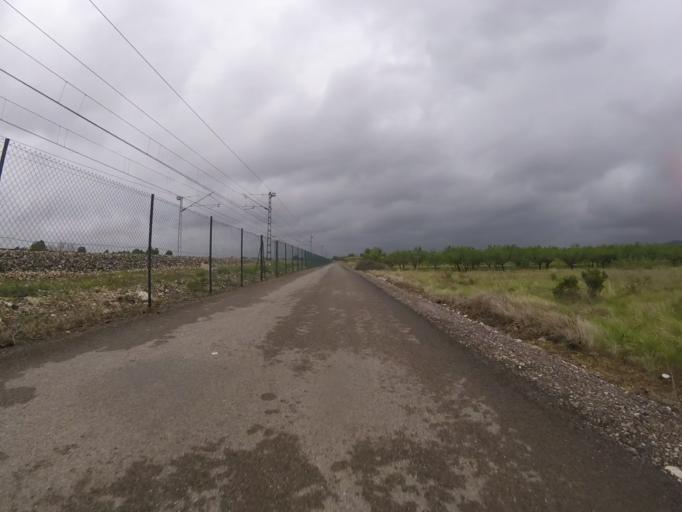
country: ES
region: Valencia
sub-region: Provincia de Castello
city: Alcala de Xivert
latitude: 40.2922
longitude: 0.2236
